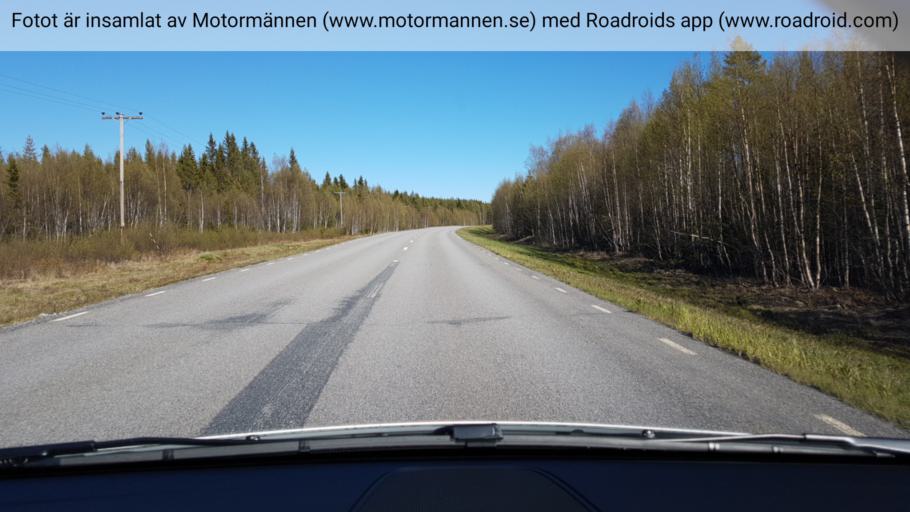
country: SE
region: Jaemtland
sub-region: Stroemsunds Kommun
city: Stroemsund
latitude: 64.3051
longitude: 15.2947
